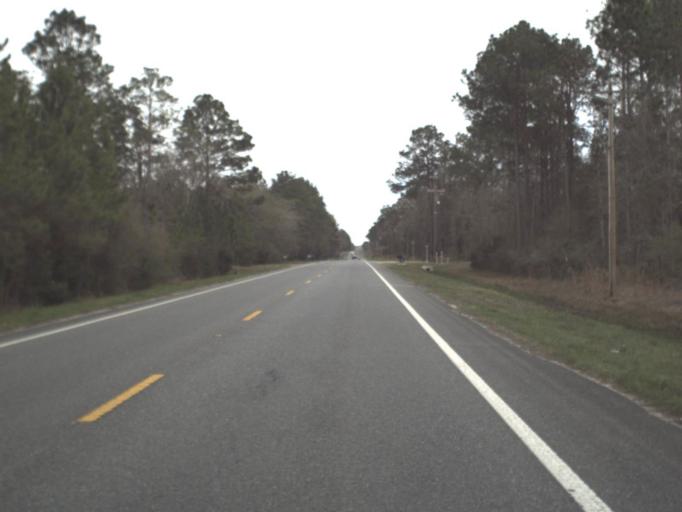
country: US
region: Florida
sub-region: Wakulla County
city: Crawfordville
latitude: 30.2814
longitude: -84.3914
